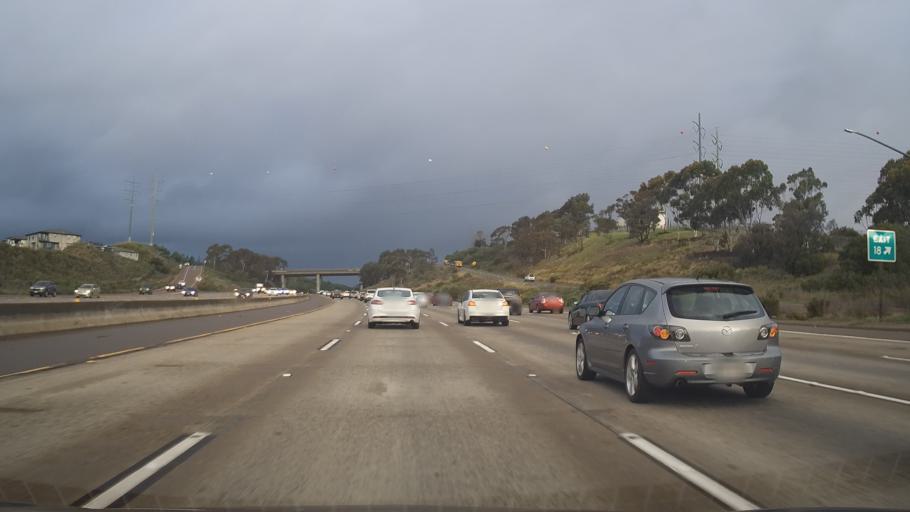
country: US
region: California
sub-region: San Diego County
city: San Diego
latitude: 32.7814
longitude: -117.1408
